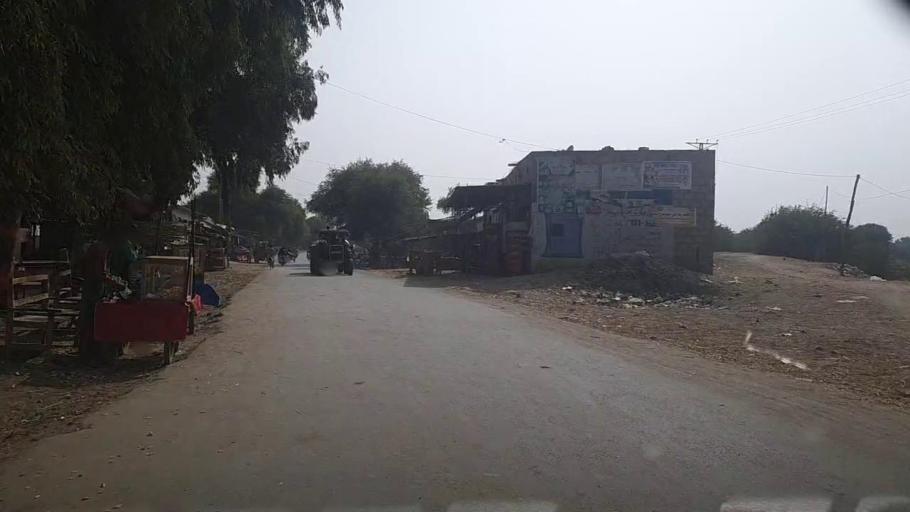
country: PK
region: Sindh
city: Kashmor
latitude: 28.4238
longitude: 69.5712
